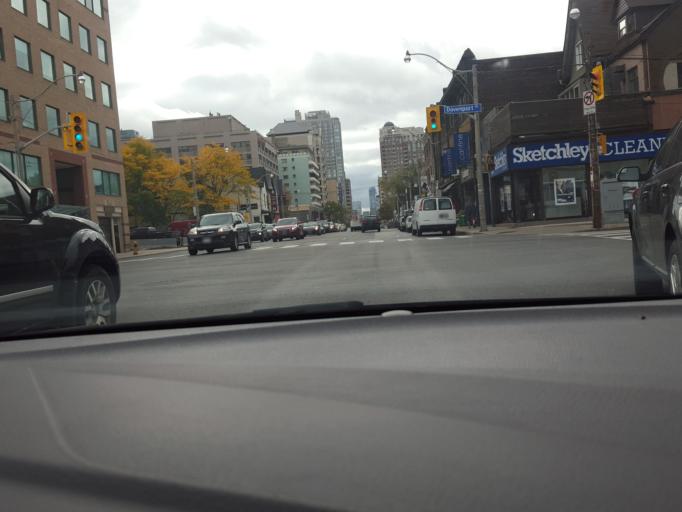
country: CA
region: Ontario
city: Toronto
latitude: 43.6748
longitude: -79.3967
